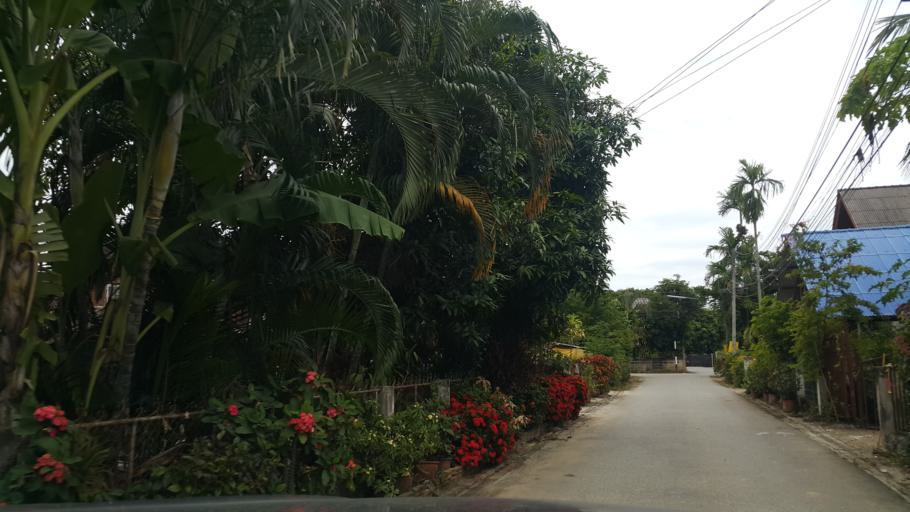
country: TH
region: Chiang Mai
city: Saraphi
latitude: 18.7072
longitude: 98.9813
